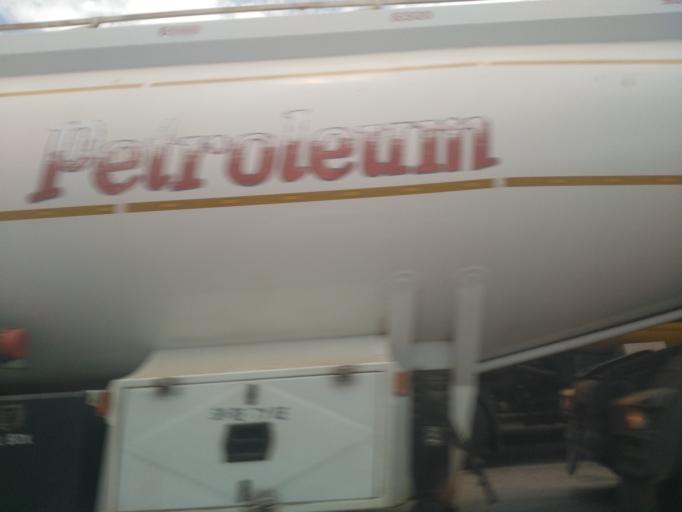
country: TZ
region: Dar es Salaam
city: Dar es Salaam
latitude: -6.8477
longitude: 39.2920
